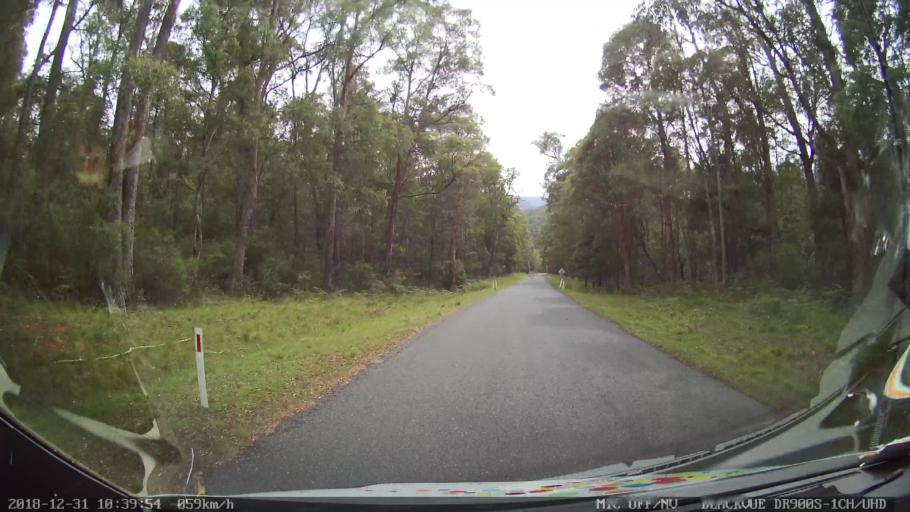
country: AU
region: New South Wales
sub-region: Snowy River
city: Jindabyne
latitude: -36.3943
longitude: 148.1777
